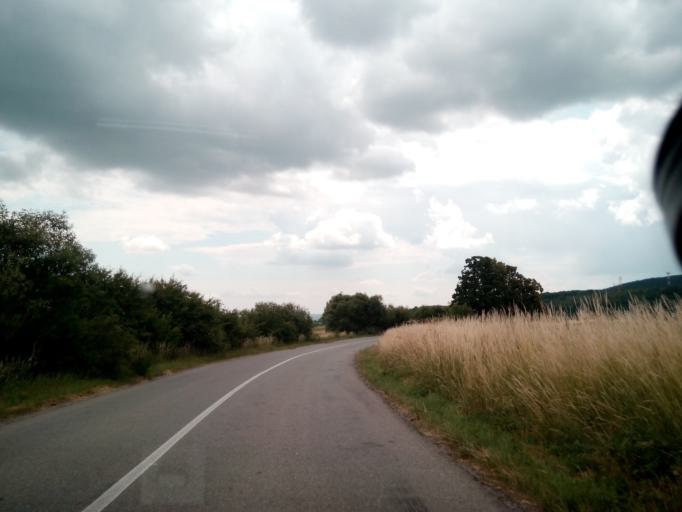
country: SK
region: Kosicky
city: Secovce
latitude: 48.6193
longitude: 21.5231
